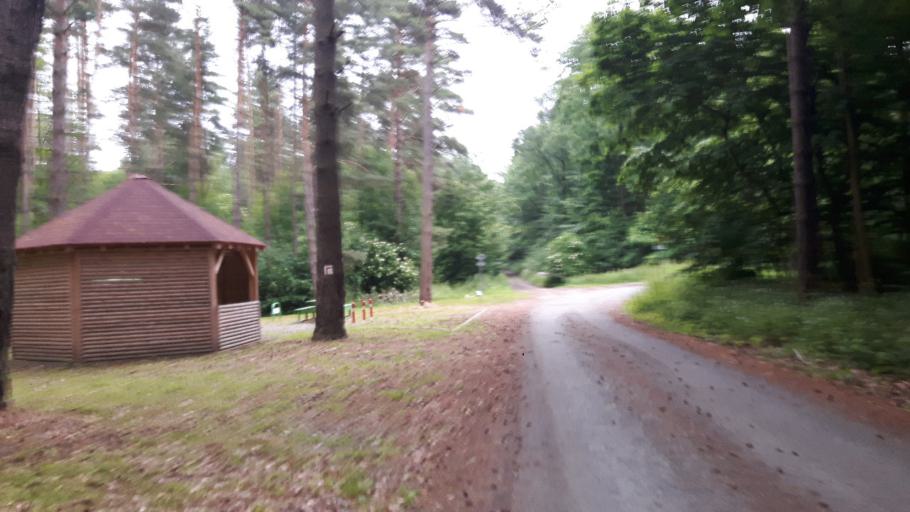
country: PL
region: Warmian-Masurian Voivodeship
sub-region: Powiat elblaski
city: Tolkmicko
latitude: 54.3362
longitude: 19.5734
